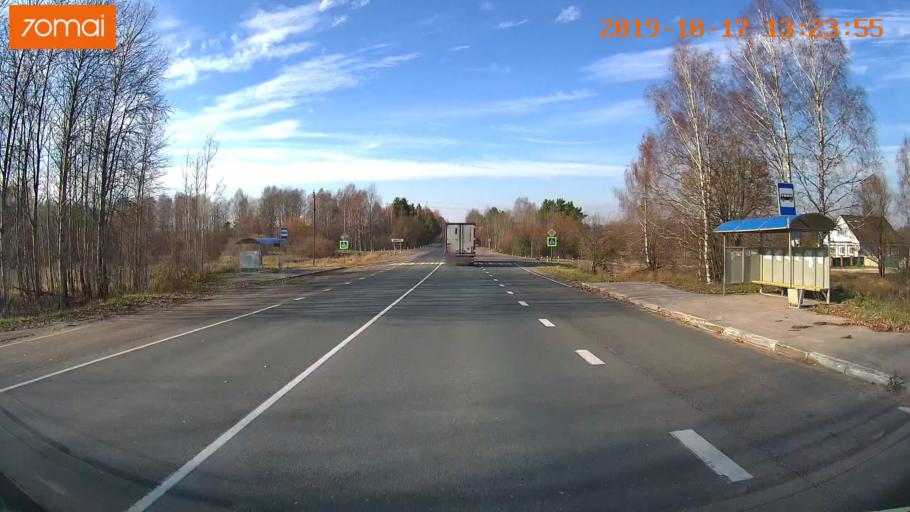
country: RU
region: Rjazan
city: Gus'-Zheleznyy
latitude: 55.0922
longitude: 40.9720
